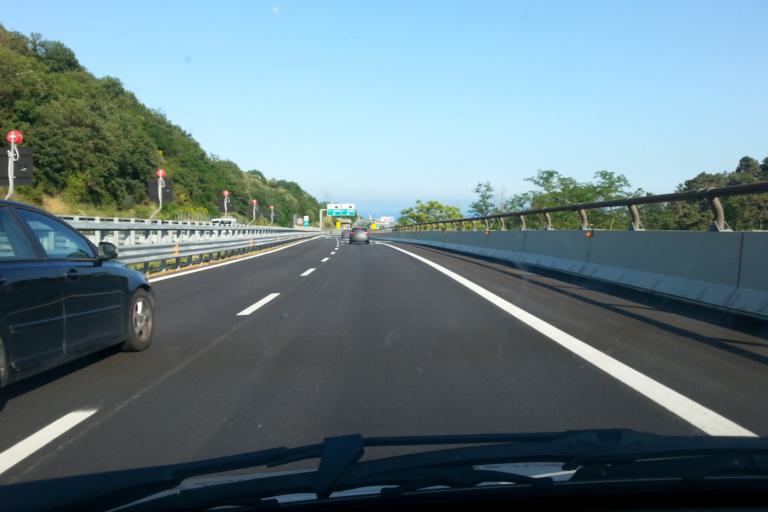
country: IT
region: Liguria
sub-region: Provincia di Savona
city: Valleggia
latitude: 44.2924
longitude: 8.4357
